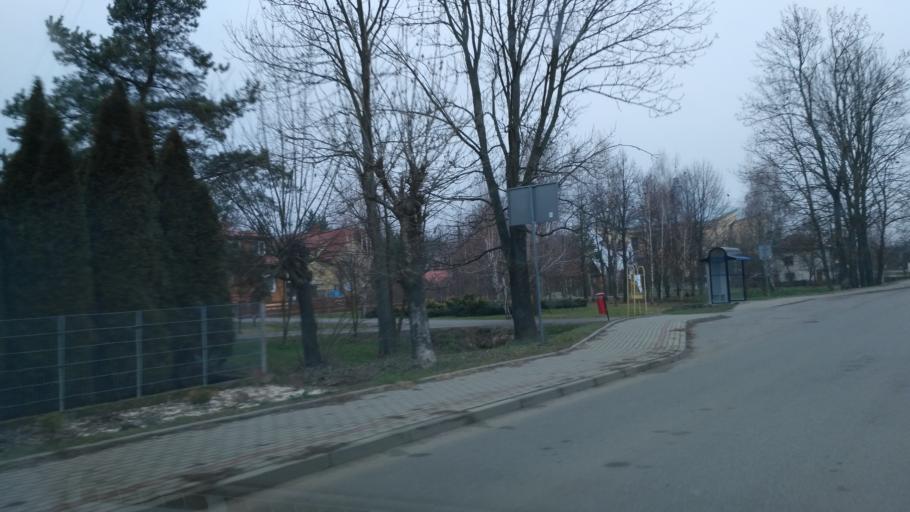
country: PL
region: Subcarpathian Voivodeship
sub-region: Powiat jaroslawski
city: Pawlosiow
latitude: 49.9924
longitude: 22.6418
